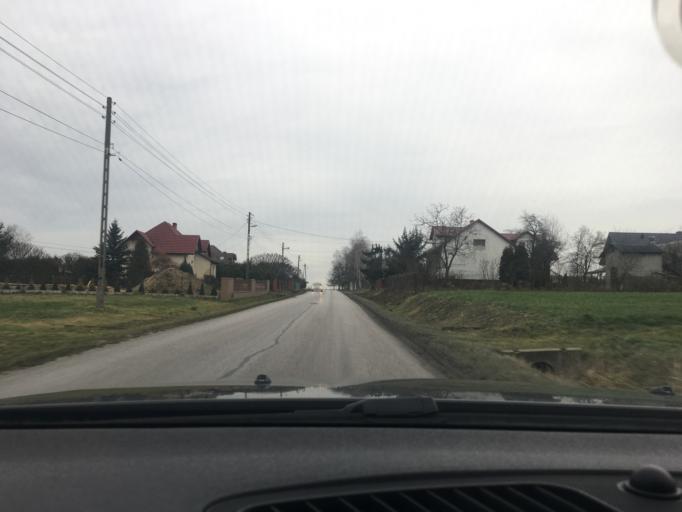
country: PL
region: Swietokrzyskie
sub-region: Powiat jedrzejowski
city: Jedrzejow
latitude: 50.6410
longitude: 20.3504
